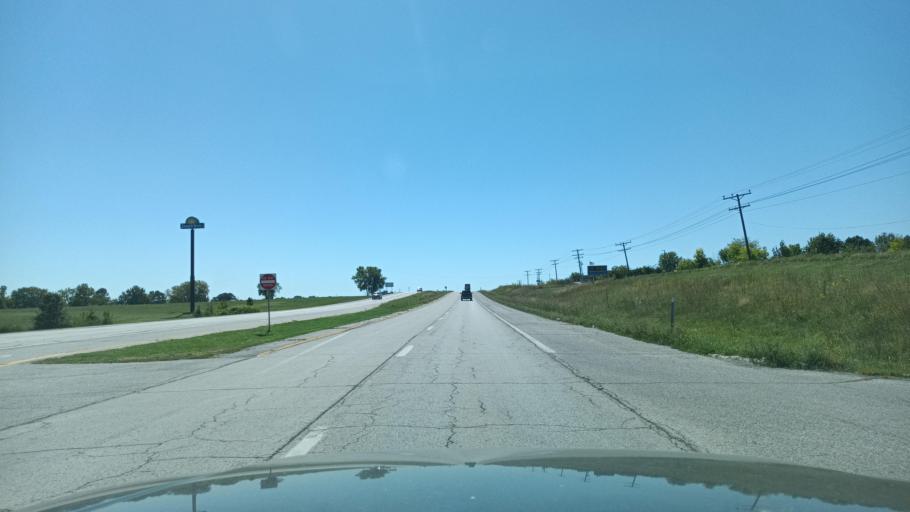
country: US
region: Missouri
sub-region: Adair County
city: Kirksville
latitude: 40.1601
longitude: -92.5722
